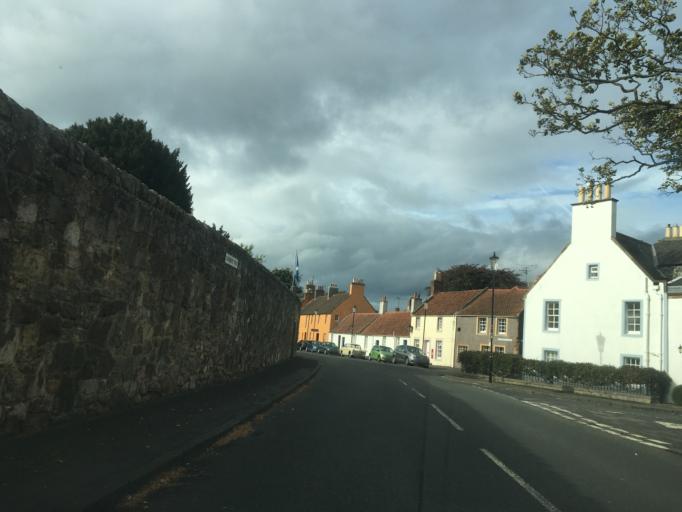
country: GB
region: Scotland
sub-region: East Lothian
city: Musselburgh
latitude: 55.9349
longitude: -3.0431
